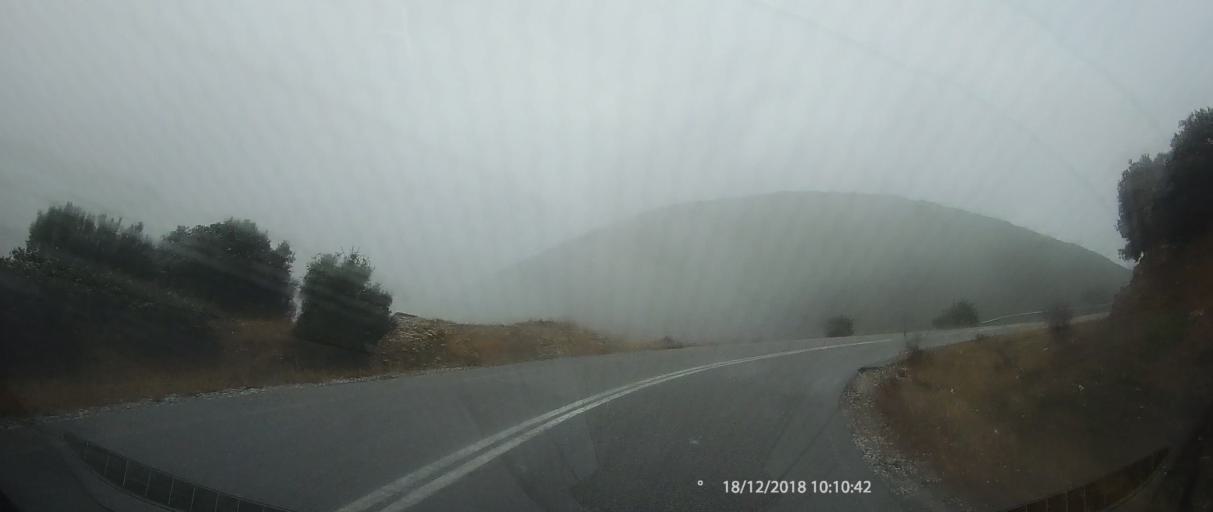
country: GR
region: Thessaly
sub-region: Nomos Larisis
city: Livadi
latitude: 40.0896
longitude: 22.2103
